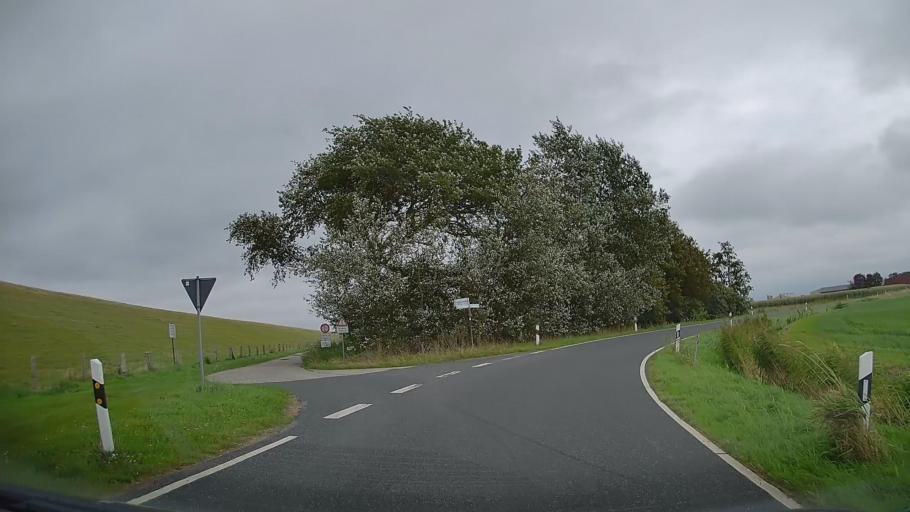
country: DE
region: Schleswig-Holstein
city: Friedrichskoog
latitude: 54.0279
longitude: 8.9262
